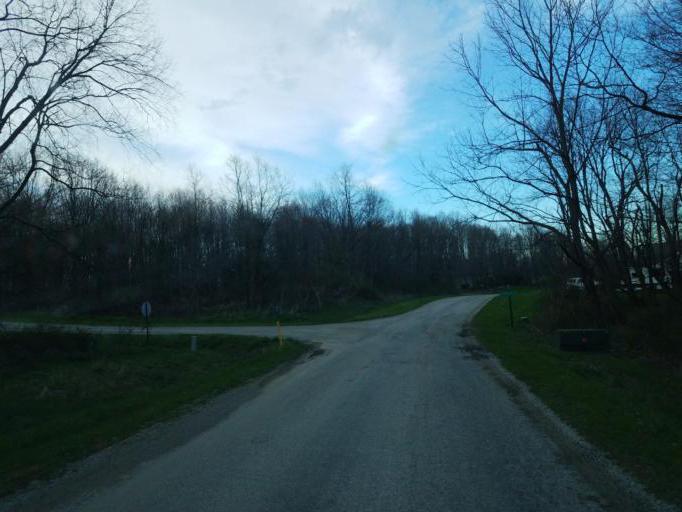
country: US
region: Ohio
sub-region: Knox County
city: Danville
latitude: 40.4631
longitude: -82.3476
